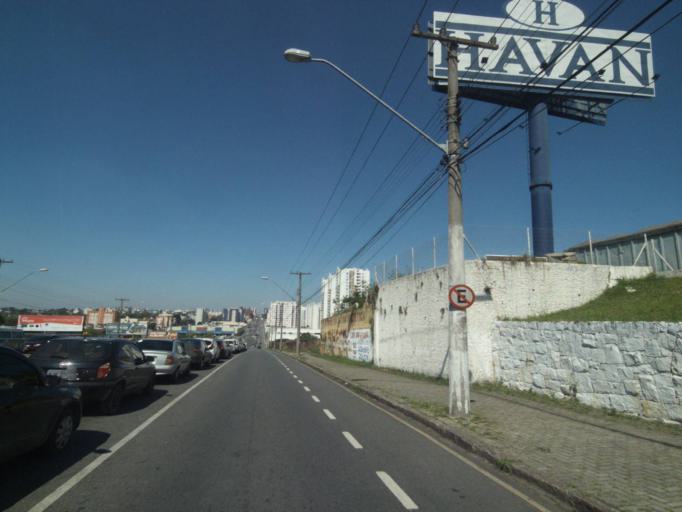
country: BR
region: Parana
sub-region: Curitiba
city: Curitiba
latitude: -25.3856
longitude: -49.2334
